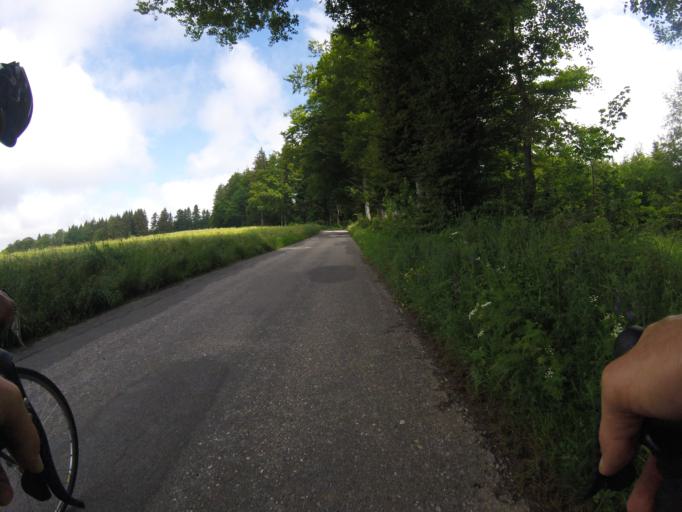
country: CH
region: Bern
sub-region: Bern-Mittelland District
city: Walkringen
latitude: 46.9608
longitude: 7.5981
